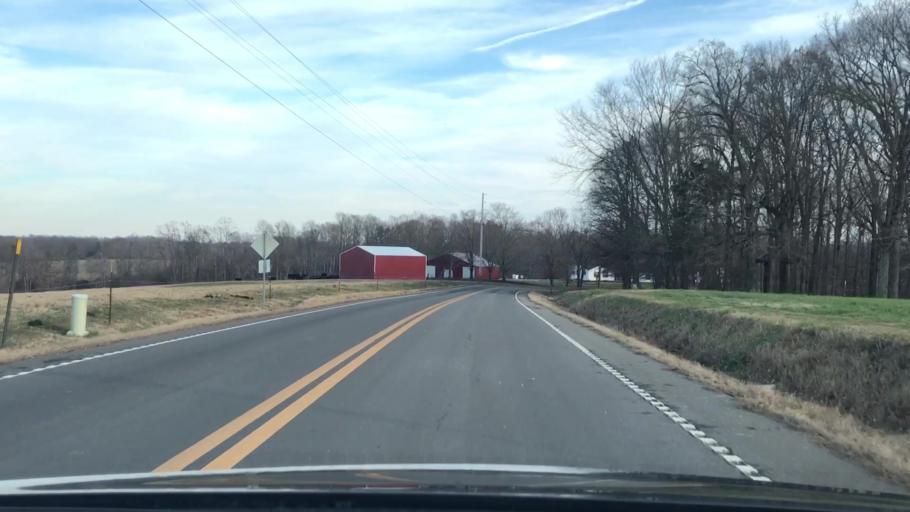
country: US
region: Tennessee
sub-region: Macon County
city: Red Boiling Springs
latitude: 36.5579
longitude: -85.8376
